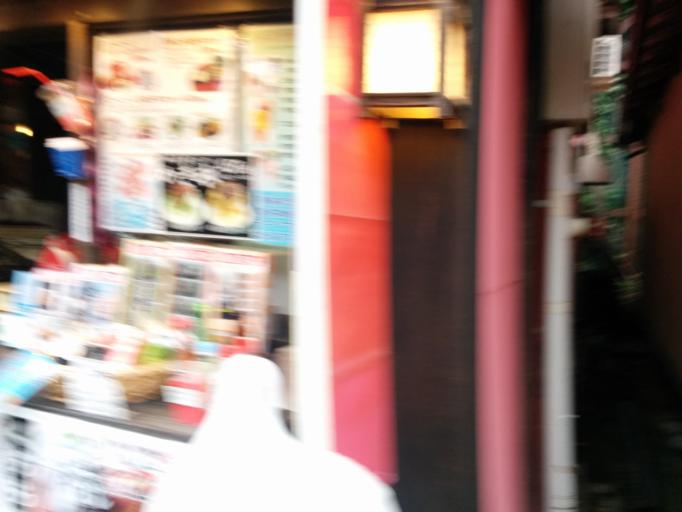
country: JP
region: Yamagata
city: Obanazawa
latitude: 38.5691
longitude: 140.5322
